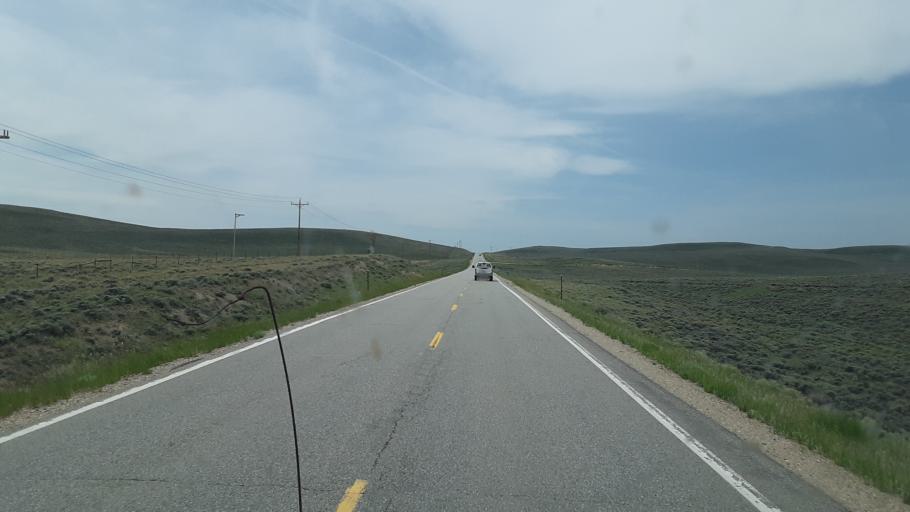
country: US
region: Colorado
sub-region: Jackson County
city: Walden
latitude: 40.6690
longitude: -106.3856
